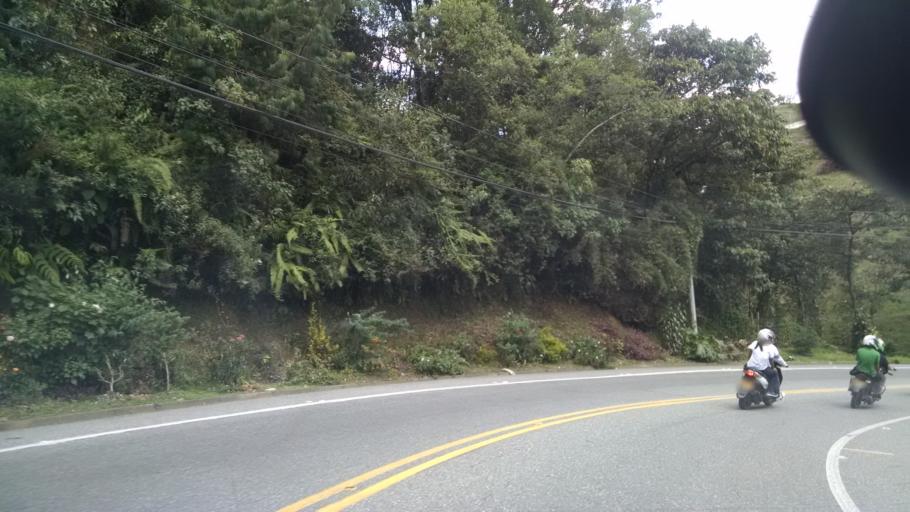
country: CO
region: Antioquia
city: Envigado
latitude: 6.1406
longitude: -75.5176
